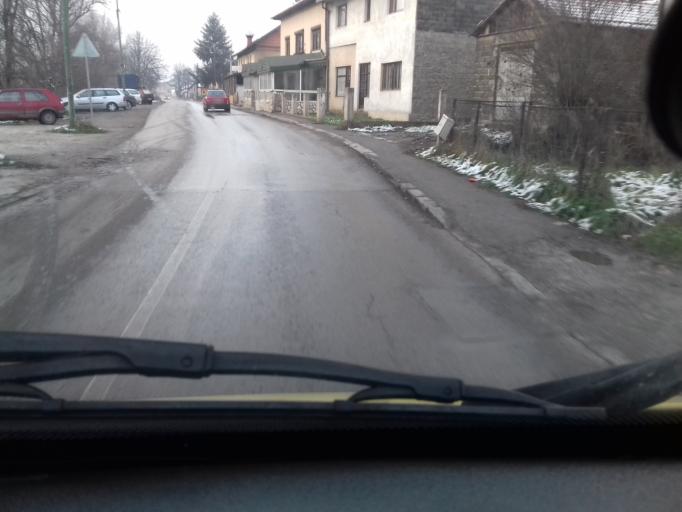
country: BA
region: Federation of Bosnia and Herzegovina
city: Visoko
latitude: 43.9936
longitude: 18.1843
